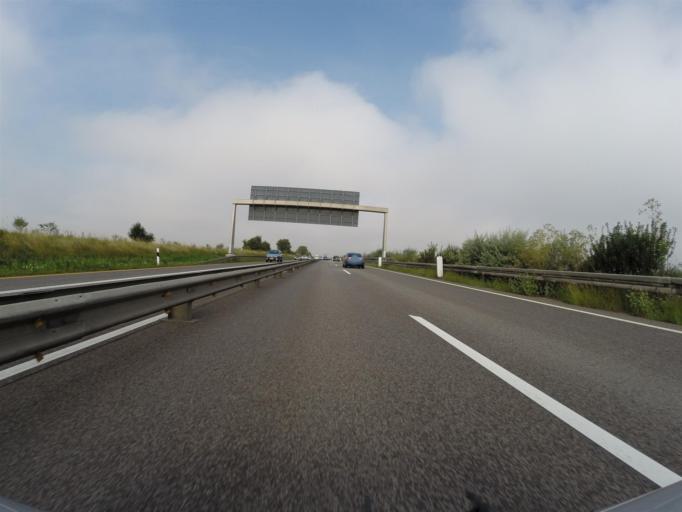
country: DE
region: Thuringia
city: Neudietendorf
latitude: 50.8934
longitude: 10.9212
